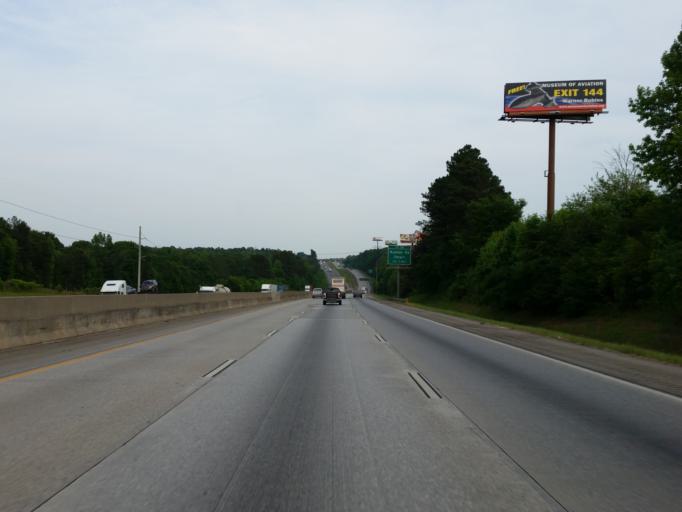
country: US
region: Georgia
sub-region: Monroe County
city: Forsyth
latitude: 33.0020
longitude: -83.8629
